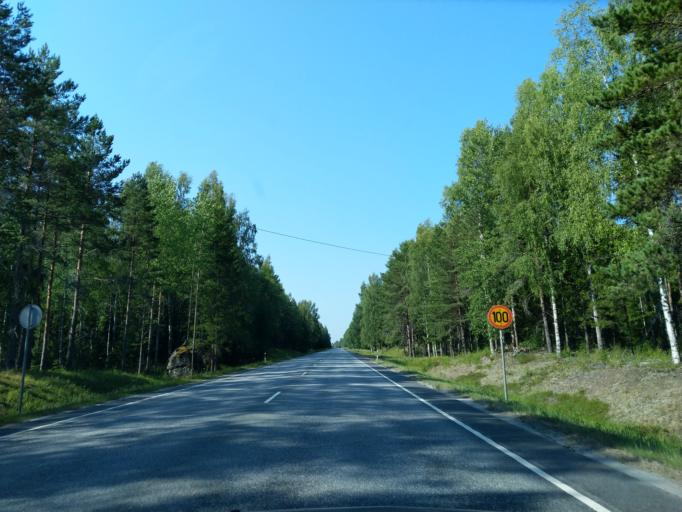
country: FI
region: Satakunta
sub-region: Pori
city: Noormarkku
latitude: 61.6233
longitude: 21.9140
